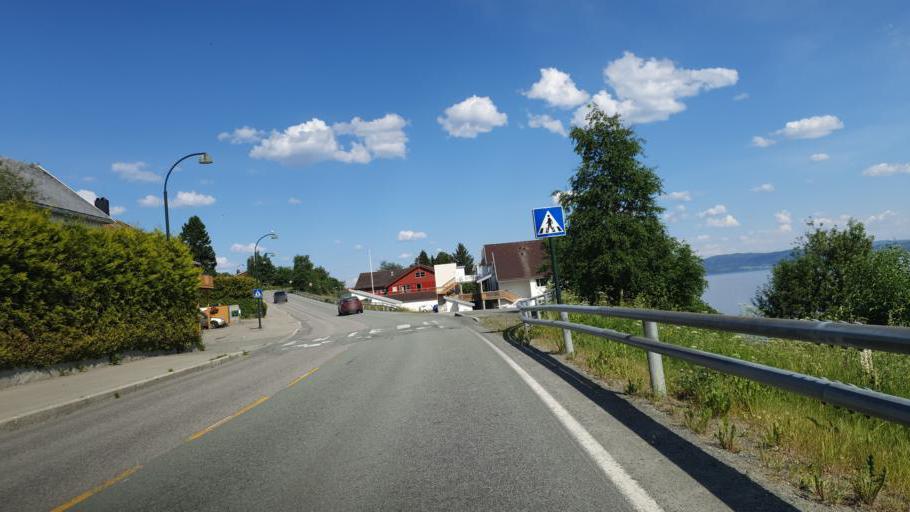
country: NO
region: Nord-Trondelag
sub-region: Leksvik
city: Leksvik
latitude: 63.6718
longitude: 10.6244
